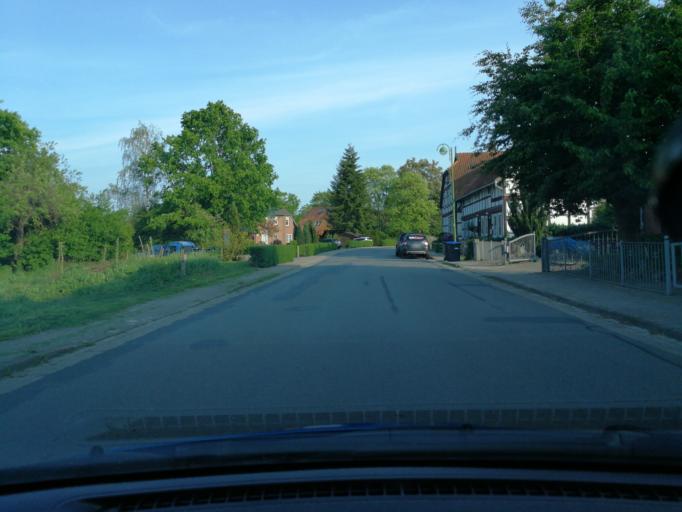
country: DE
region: Lower Saxony
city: Scharnebeck
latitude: 53.2950
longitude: 10.5076
